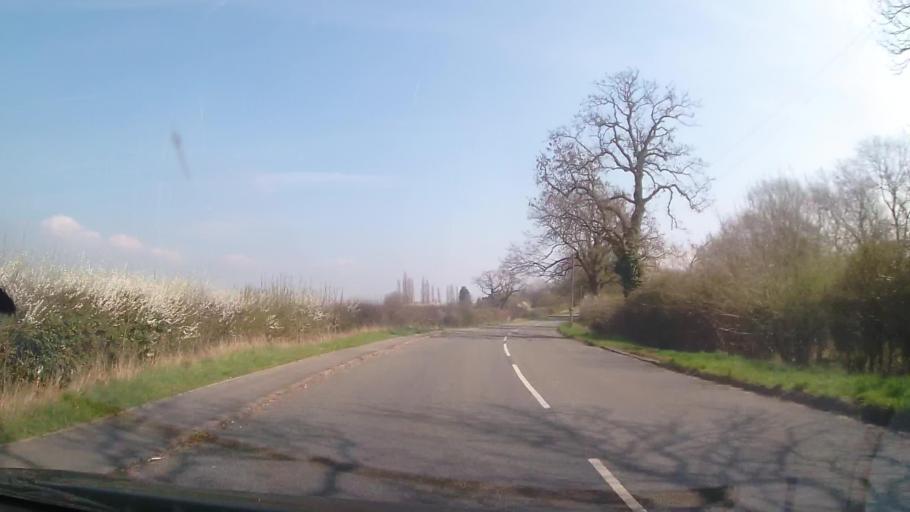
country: GB
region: England
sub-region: Leicestershire
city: Anstey
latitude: 52.6799
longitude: -1.2083
